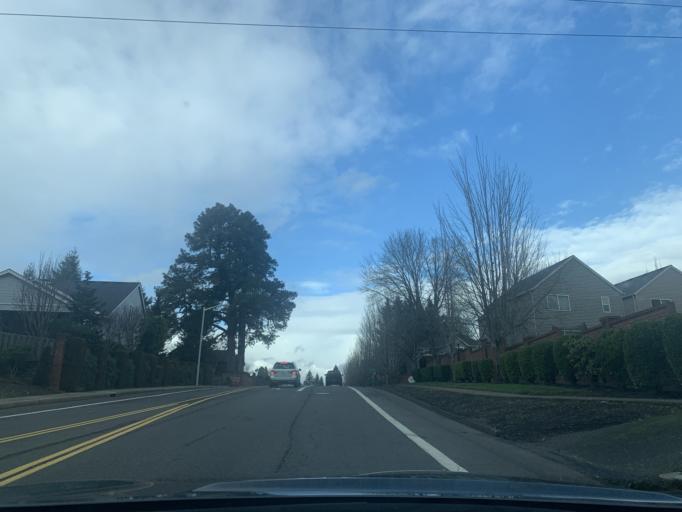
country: US
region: Oregon
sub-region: Washington County
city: Oak Hills
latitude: 45.5643
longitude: -122.8354
